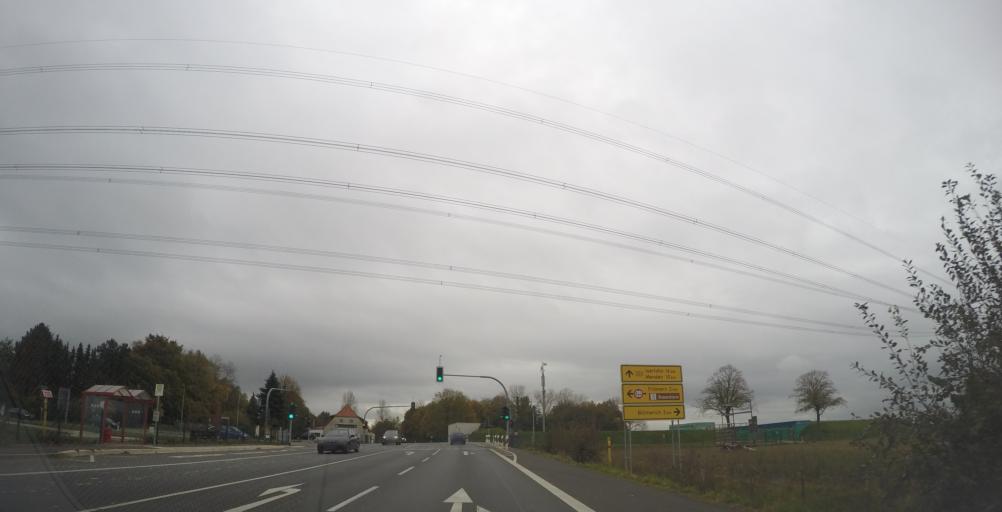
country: DE
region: North Rhine-Westphalia
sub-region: Regierungsbezirk Arnsberg
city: Unna
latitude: 51.5007
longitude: 7.7031
